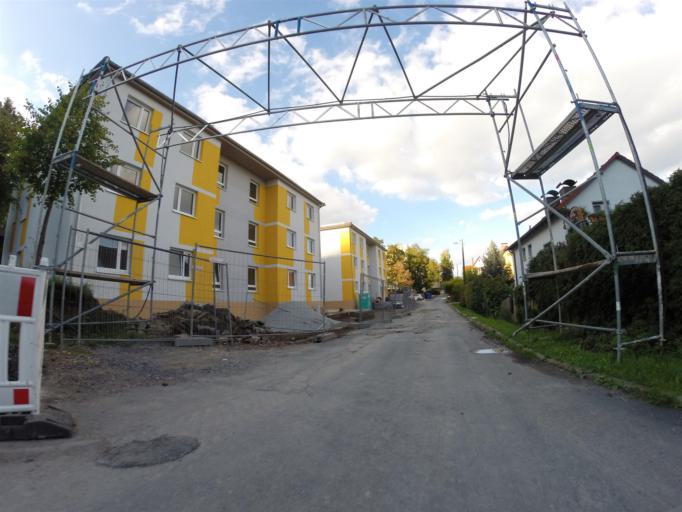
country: DE
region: Thuringia
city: Jena
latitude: 50.9376
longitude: 11.5837
